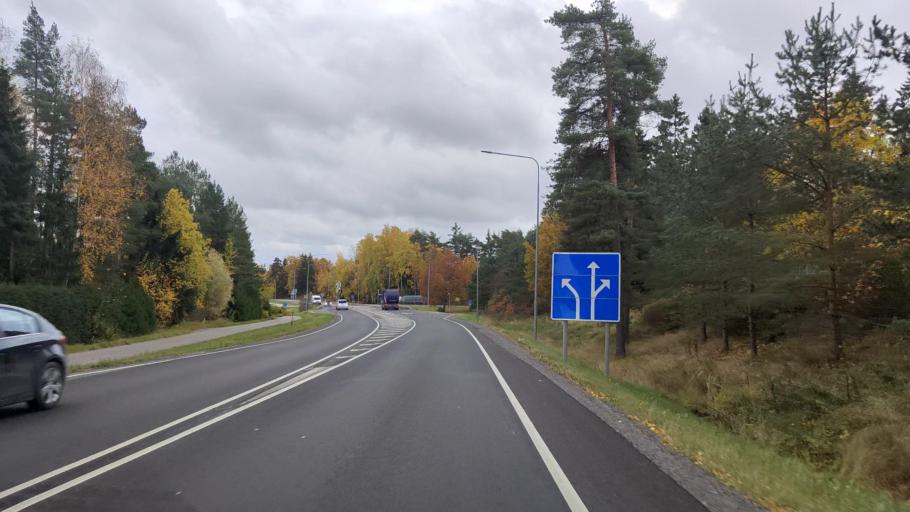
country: FI
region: Varsinais-Suomi
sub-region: Turku
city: Kaarina
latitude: 60.4477
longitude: 22.3739
